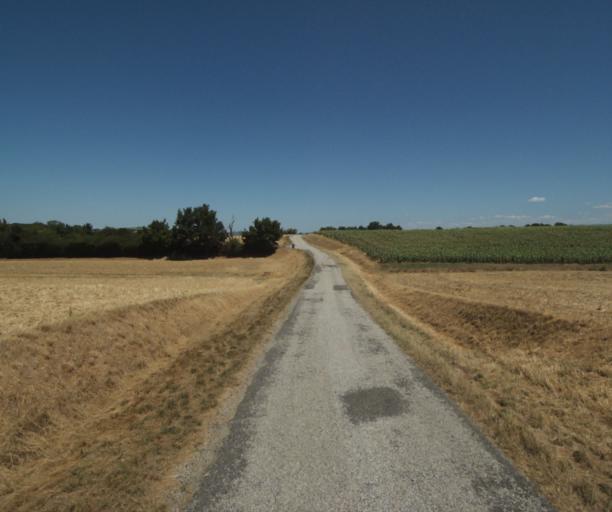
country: FR
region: Midi-Pyrenees
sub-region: Departement de la Haute-Garonne
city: Saint-Felix-Lauragais
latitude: 43.4725
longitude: 1.9144
